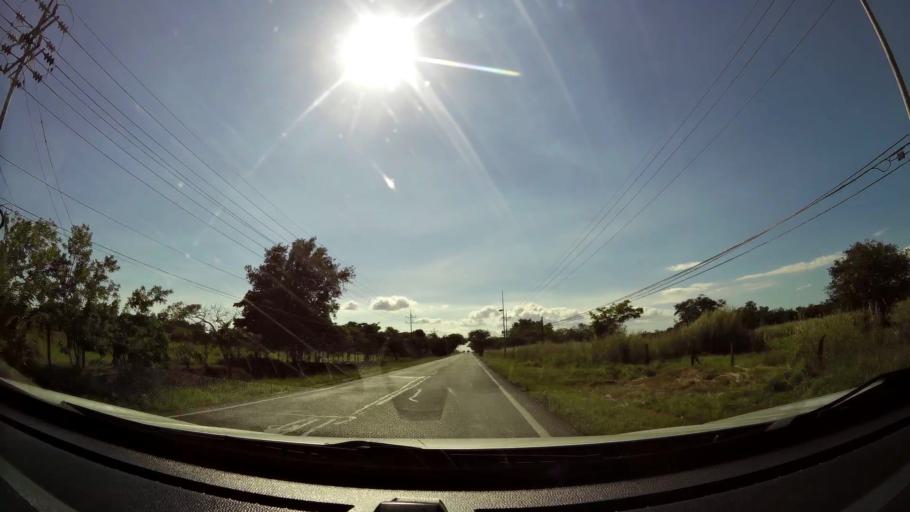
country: CR
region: Guanacaste
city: Liberia
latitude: 10.6096
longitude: -85.5017
